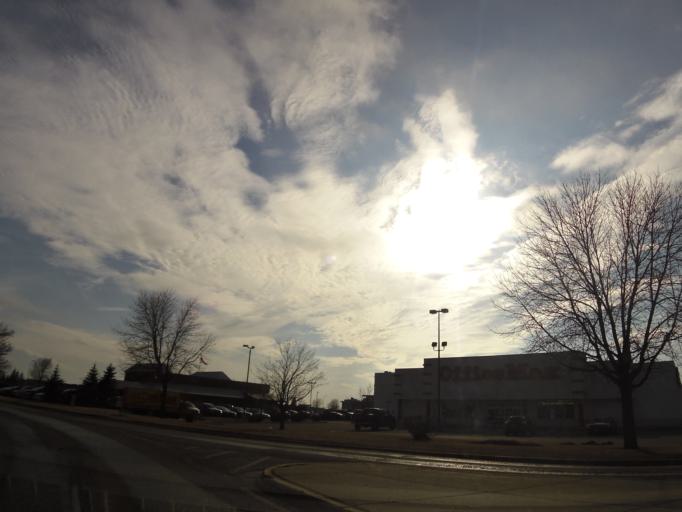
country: US
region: North Dakota
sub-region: Grand Forks County
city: Grand Forks
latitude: 47.8911
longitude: -97.0731
